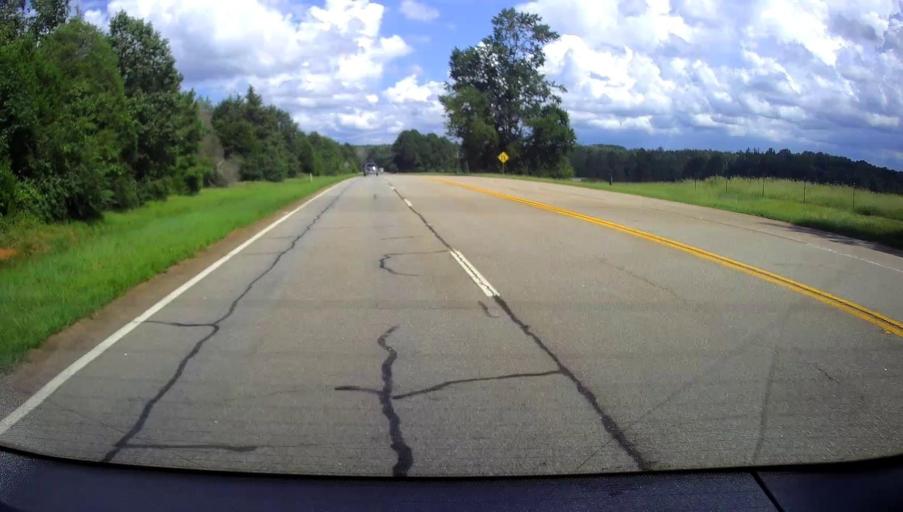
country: US
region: Georgia
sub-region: Upson County
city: Thomaston
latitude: 32.9204
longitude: -84.1967
